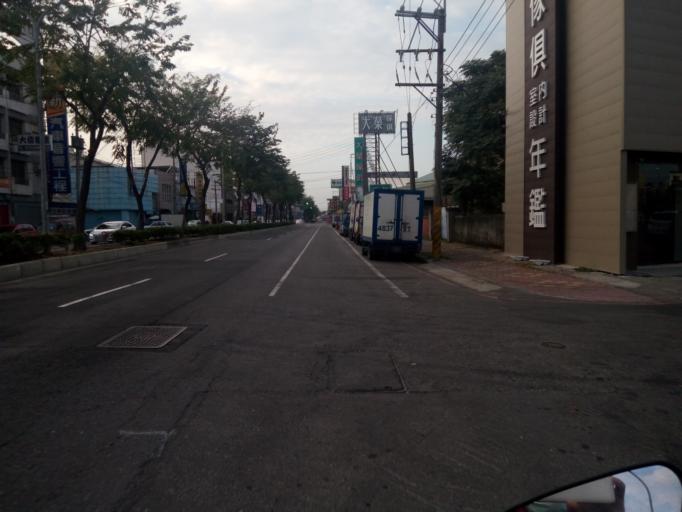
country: TW
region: Taiwan
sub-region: Chiayi
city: Jiayi Shi
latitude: 23.4813
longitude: 120.4283
